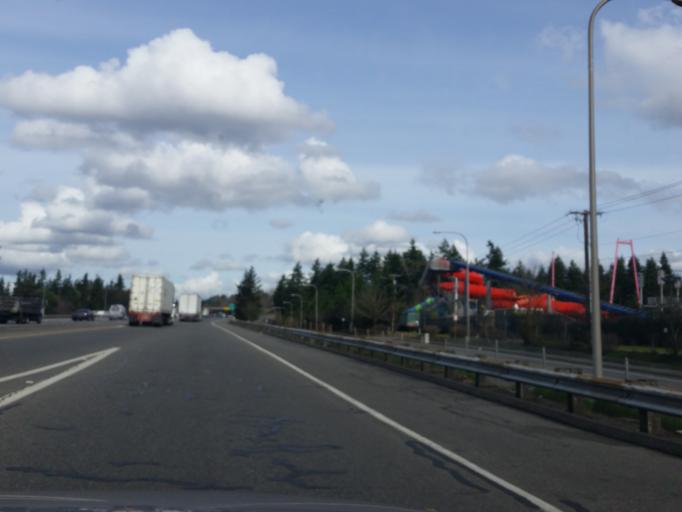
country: US
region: Washington
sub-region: Pierce County
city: Milton
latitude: 47.2733
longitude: -122.3137
